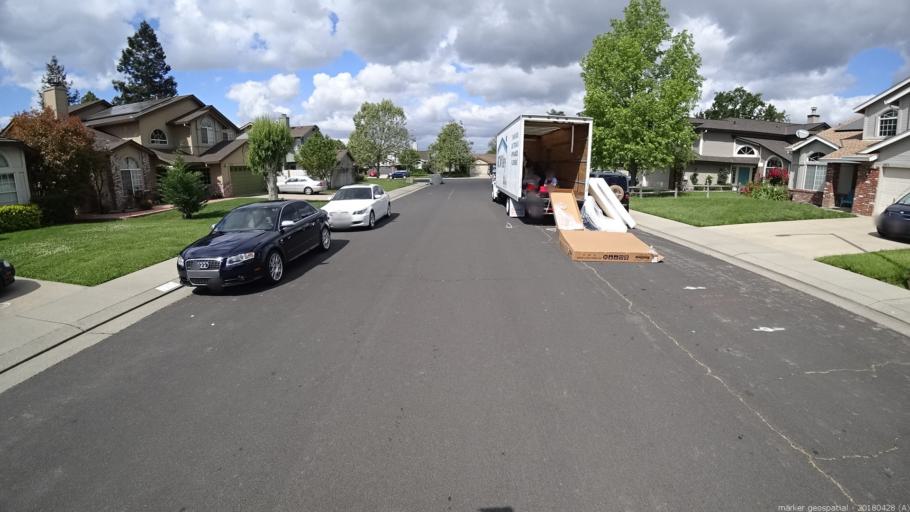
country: US
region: California
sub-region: Yolo County
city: West Sacramento
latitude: 38.5417
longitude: -121.5573
